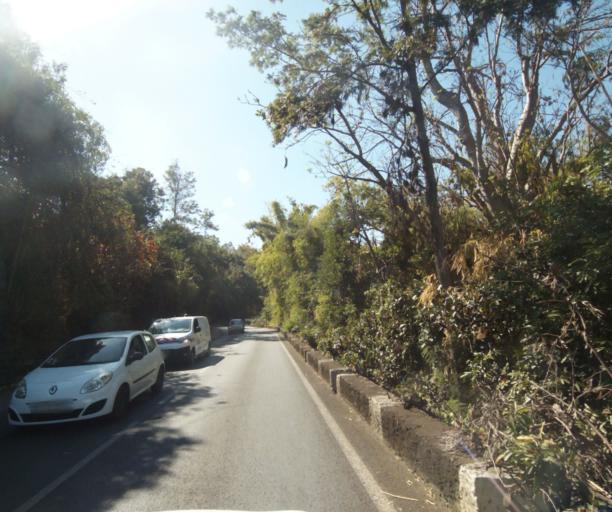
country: RE
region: Reunion
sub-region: Reunion
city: Saint-Paul
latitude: -20.9934
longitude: 55.3306
